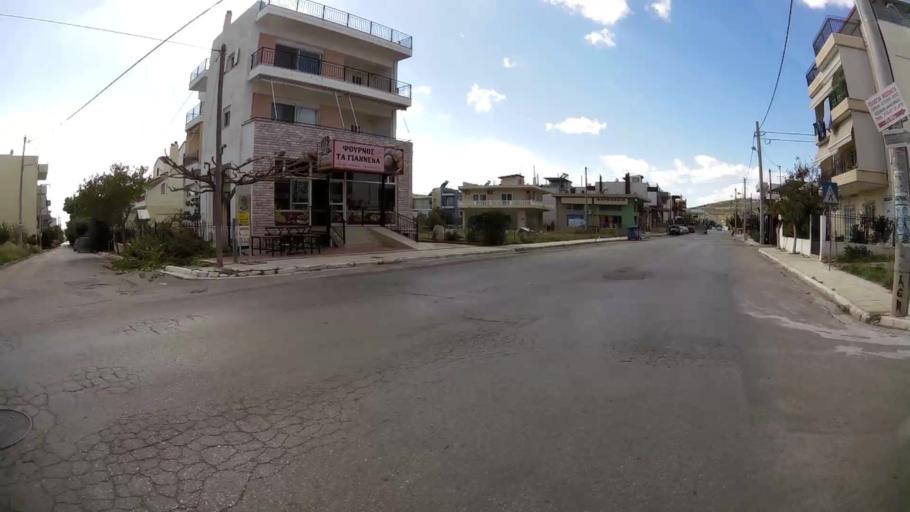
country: GR
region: Attica
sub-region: Nomarchia Anatolikis Attikis
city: Acharnes
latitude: 38.0975
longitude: 23.7321
